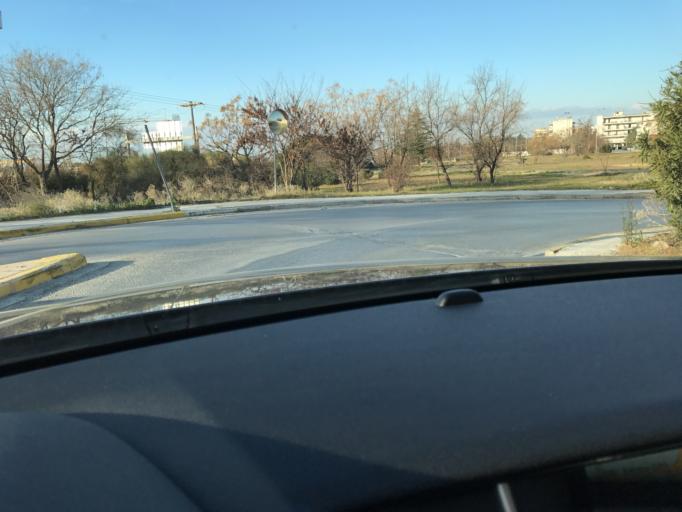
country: GR
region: Central Macedonia
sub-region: Nomos Thessalonikis
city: Efkarpia
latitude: 40.6798
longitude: 22.9552
